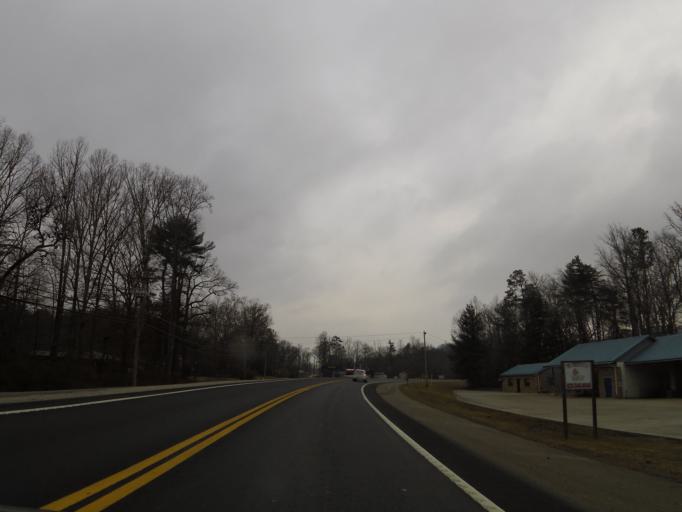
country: US
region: Tennessee
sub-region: Morgan County
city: Wartburg
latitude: 36.0979
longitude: -84.5818
